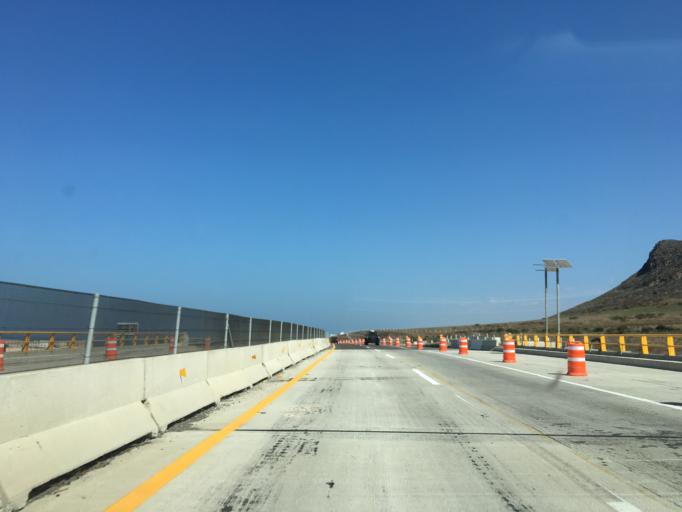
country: MX
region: Baja California
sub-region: Playas de Rosarito
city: Ciudad Morelos
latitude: 32.2848
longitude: -117.0307
